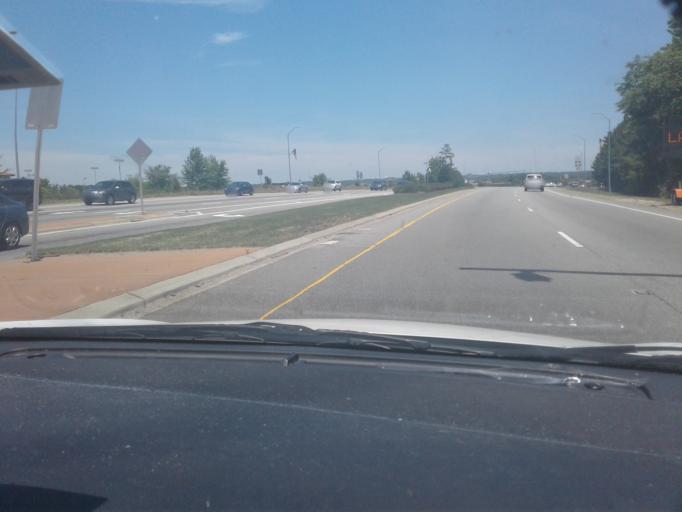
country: US
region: North Carolina
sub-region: Wake County
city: Holly Springs
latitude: 35.6578
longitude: -78.8485
